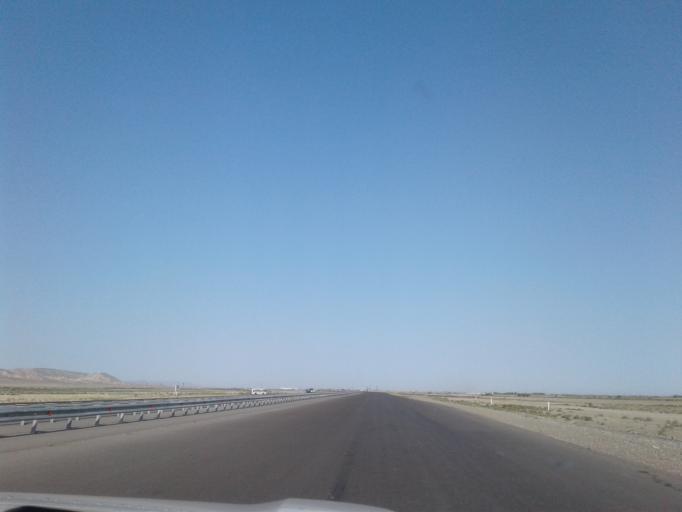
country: TM
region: Balkan
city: Serdar
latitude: 38.9385
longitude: 56.4337
